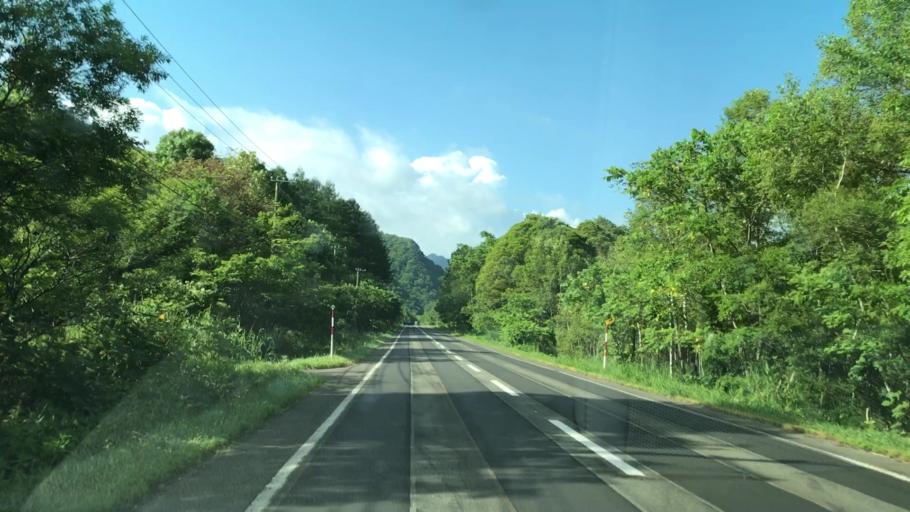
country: JP
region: Hokkaido
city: Shizunai-furukawacho
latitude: 42.8295
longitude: 142.4161
